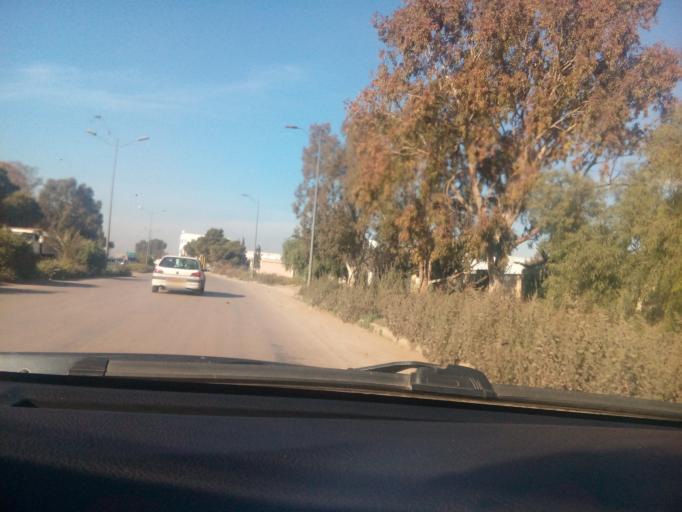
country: DZ
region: Oran
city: Es Senia
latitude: 35.6360
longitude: -0.6015
